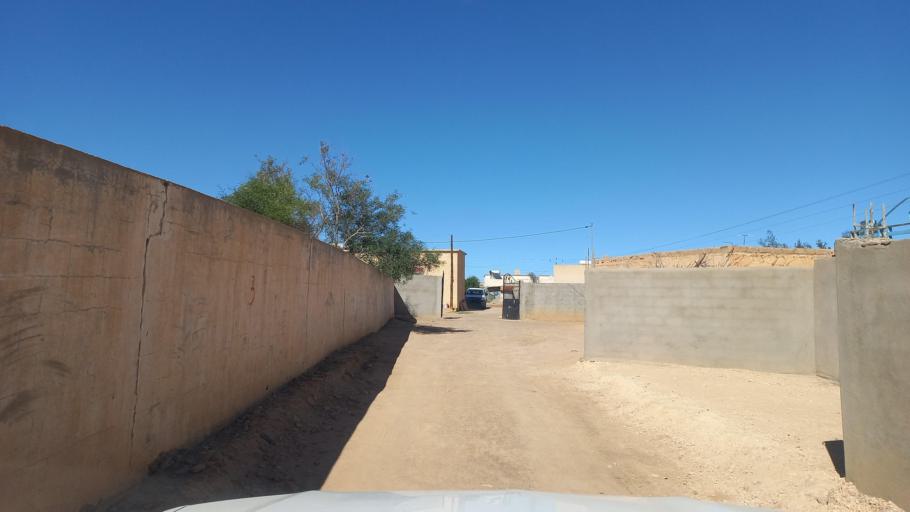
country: TN
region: Al Qasrayn
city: Sbiba
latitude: 35.3620
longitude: 9.0923
